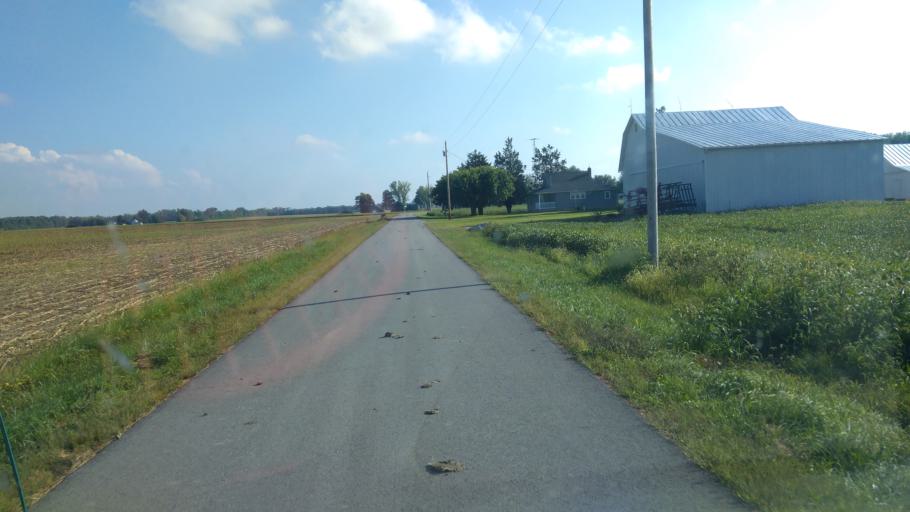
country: US
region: Ohio
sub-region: Hardin County
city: Forest
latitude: 40.7333
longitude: -83.4776
